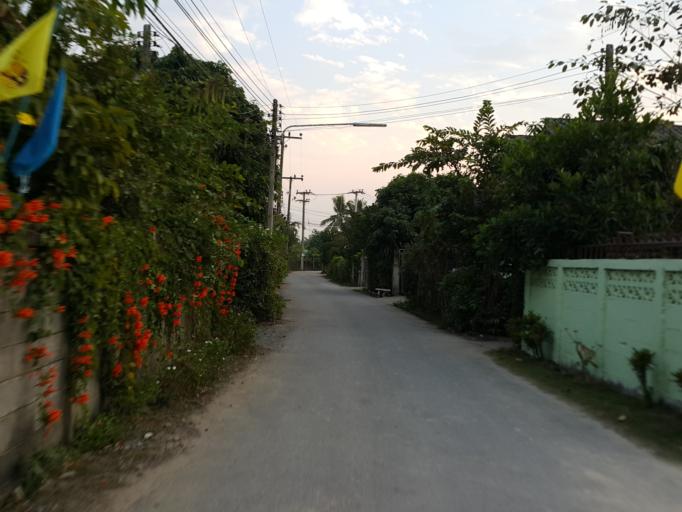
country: TH
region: Chiang Mai
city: San Sai
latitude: 18.8385
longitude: 99.1084
